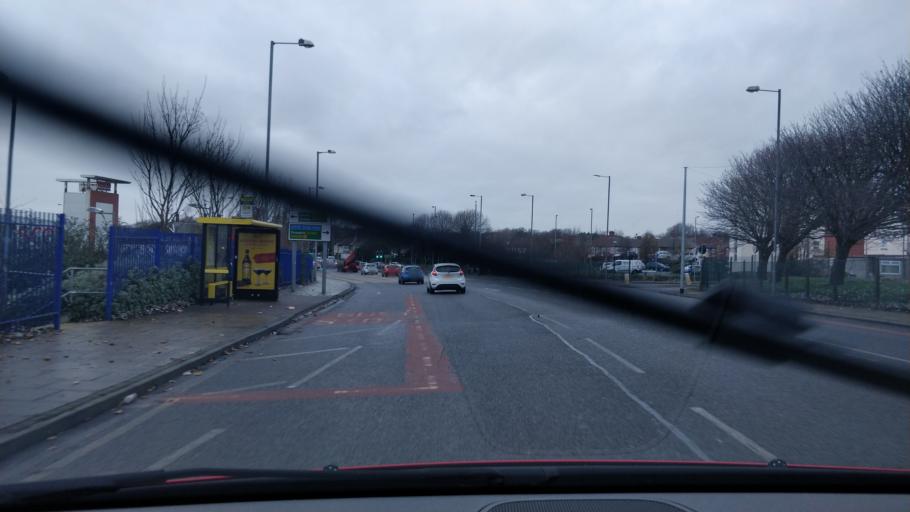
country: GB
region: England
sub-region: Sefton
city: Litherland
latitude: 53.4690
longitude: -2.9964
